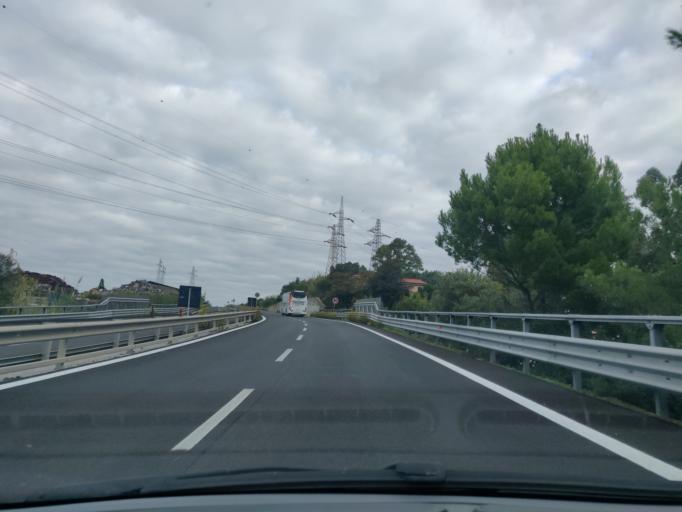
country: IT
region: Latium
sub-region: Citta metropolitana di Roma Capitale
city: Civitavecchia
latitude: 42.1083
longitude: 11.7926
